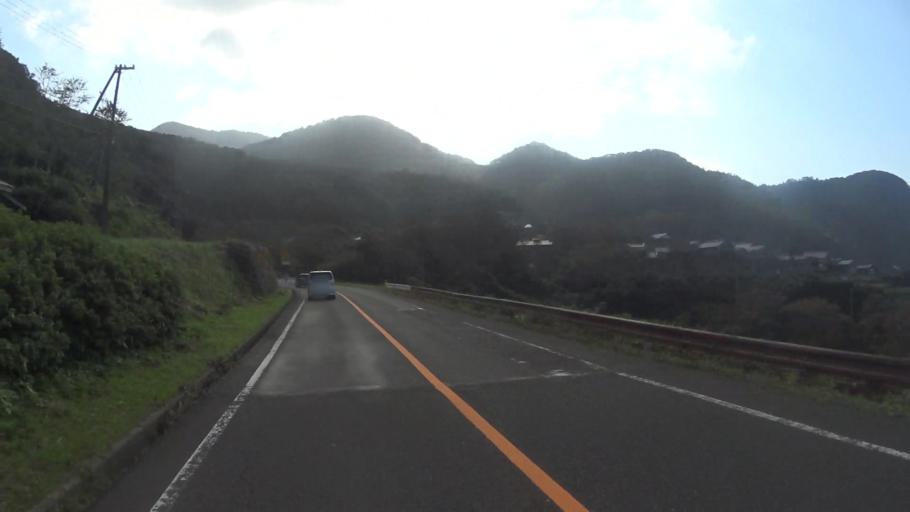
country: JP
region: Kyoto
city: Miyazu
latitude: 35.7484
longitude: 135.1468
